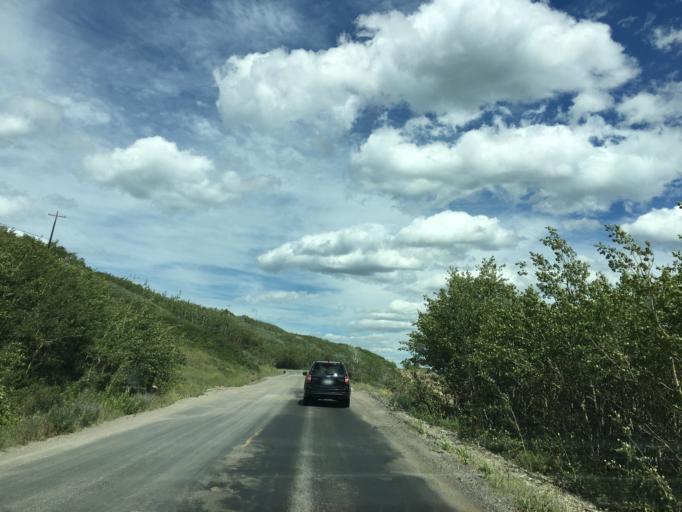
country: CA
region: Alberta
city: Cardston
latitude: 48.8262
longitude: -113.5607
